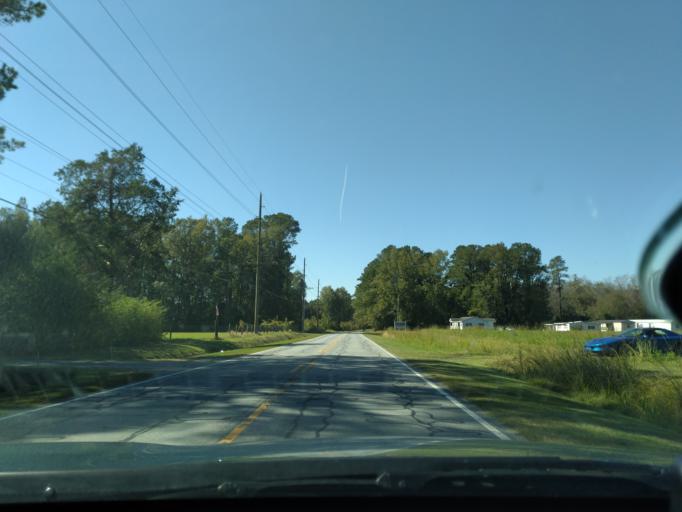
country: US
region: North Carolina
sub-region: Beaufort County
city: River Road
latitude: 35.5639
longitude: -76.9886
